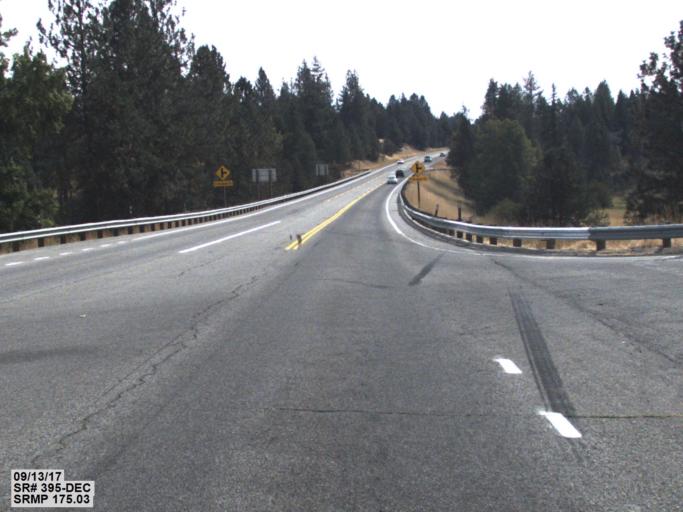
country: US
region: Washington
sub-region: Spokane County
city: Deer Park
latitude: 47.8880
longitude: -117.4250
